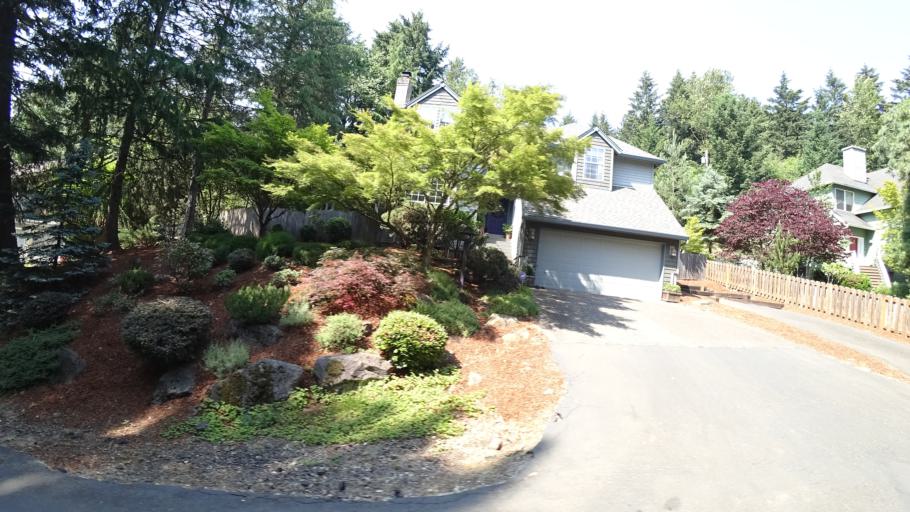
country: US
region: Oregon
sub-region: Clackamas County
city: Happy Valley
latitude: 45.4428
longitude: -122.5542
